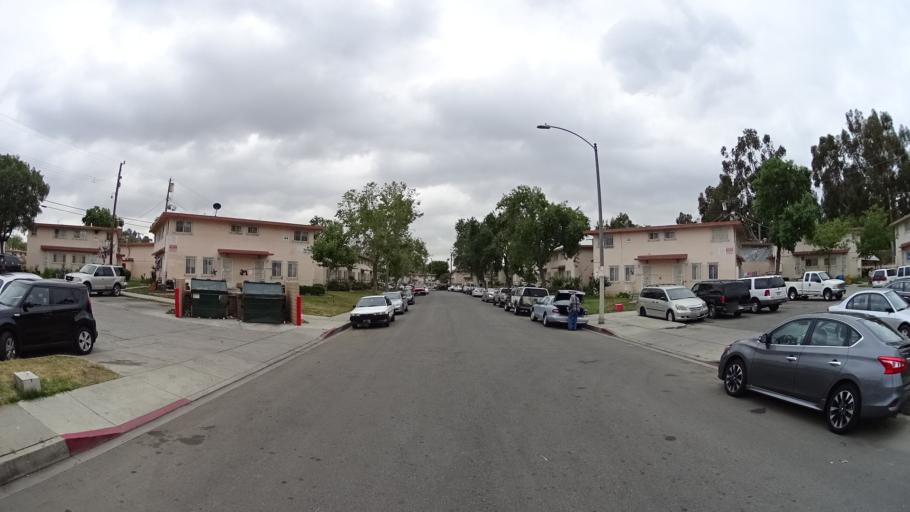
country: US
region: California
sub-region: Los Angeles County
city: Boyle Heights
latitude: 34.0598
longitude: -118.1936
